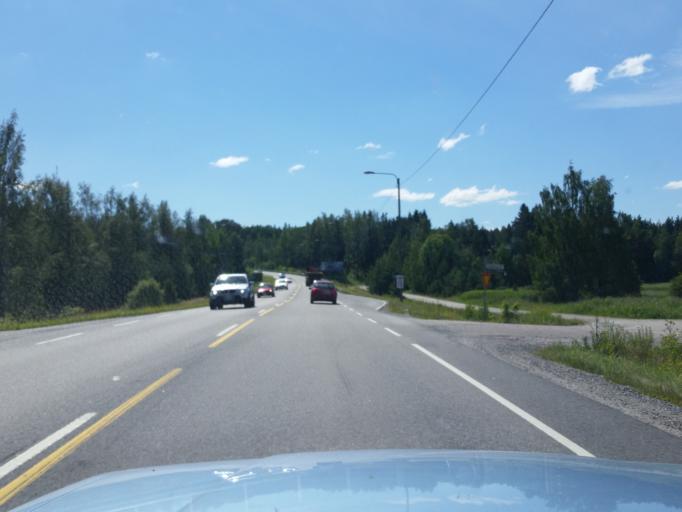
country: FI
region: Varsinais-Suomi
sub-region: Turku
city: Kaarina
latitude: 60.3591
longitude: 22.3576
